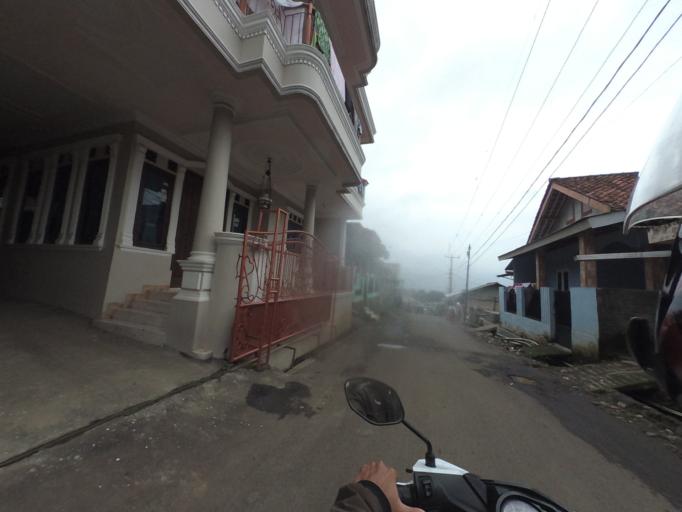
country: ID
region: West Java
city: Bogor
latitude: -6.6211
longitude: 106.7459
